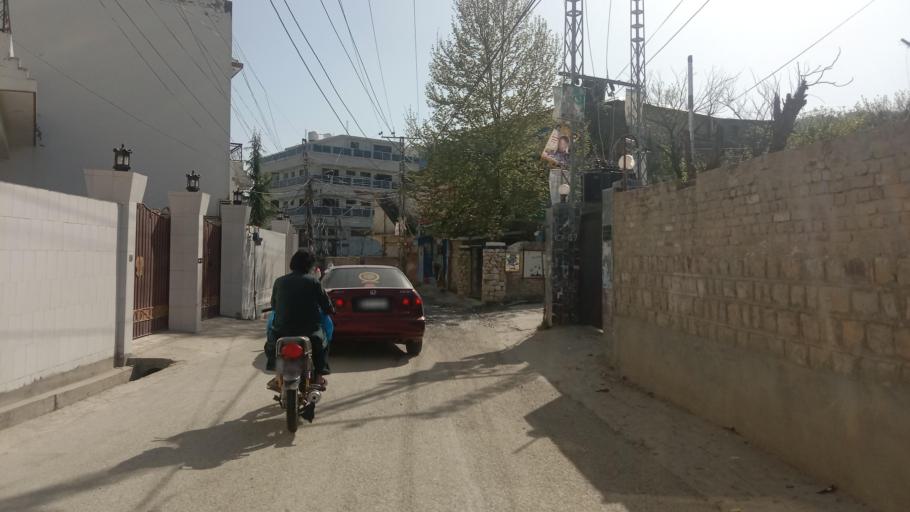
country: PK
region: Khyber Pakhtunkhwa
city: Abbottabad
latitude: 34.1723
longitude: 73.2236
